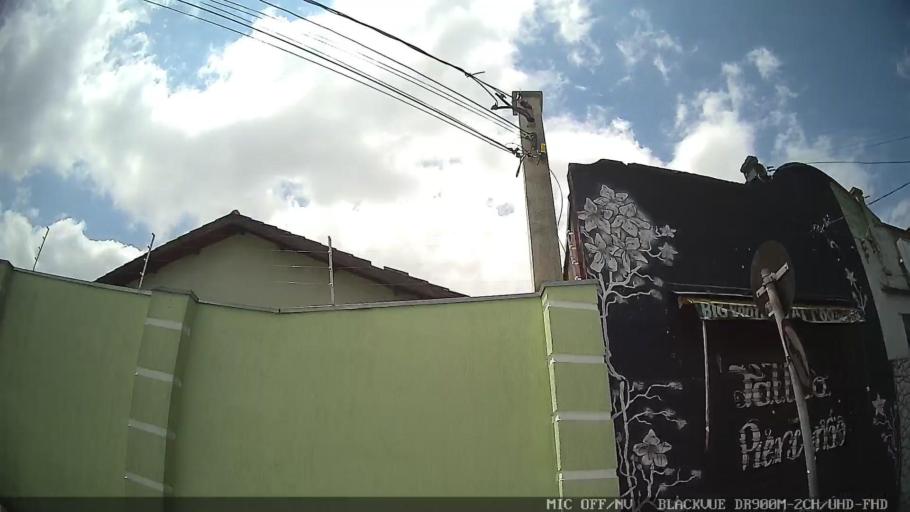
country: BR
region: Sao Paulo
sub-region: Guarulhos
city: Guarulhos
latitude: -23.5338
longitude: -46.4927
